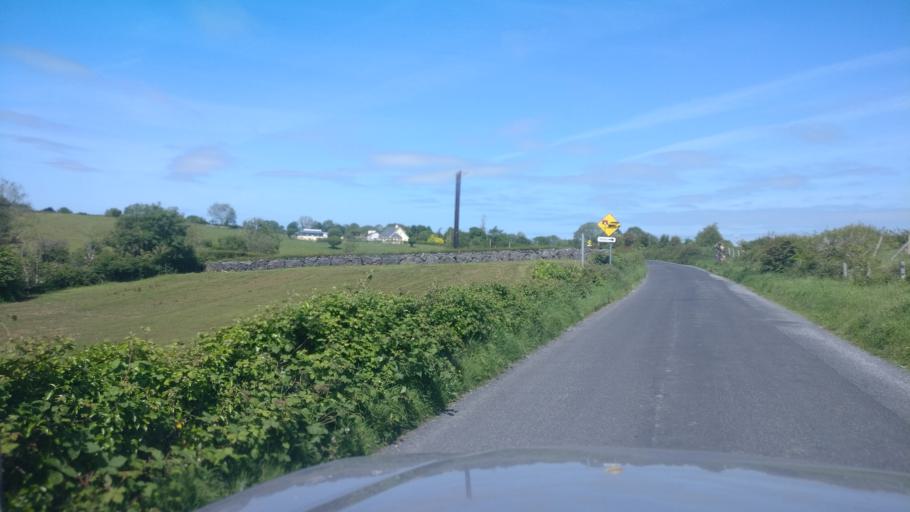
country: IE
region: Connaught
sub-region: County Galway
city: Gort
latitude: 53.0919
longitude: -8.8065
